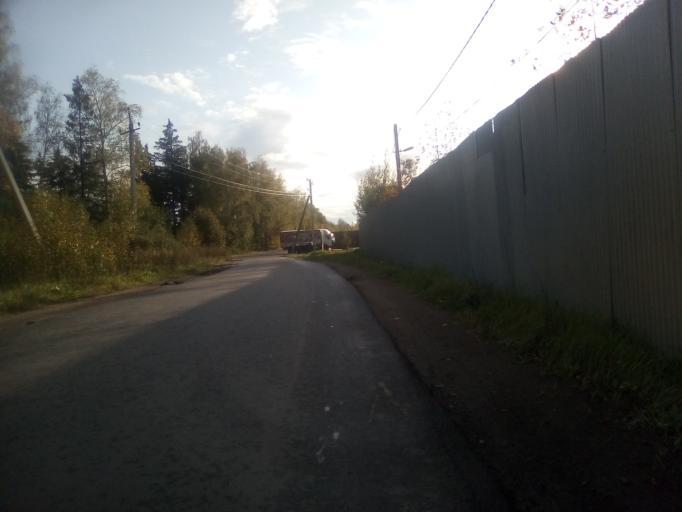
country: RU
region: Moskovskaya
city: Krasnoznamensk
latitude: 55.5730
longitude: 37.0236
